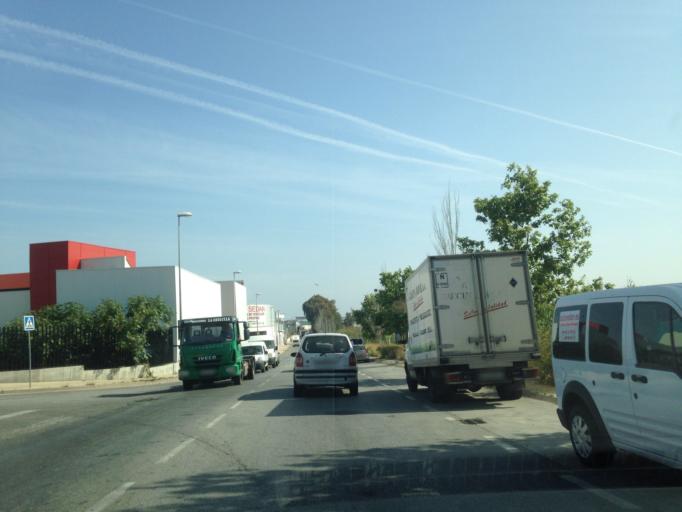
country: ES
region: Andalusia
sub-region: Provincia de Malaga
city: Malaga
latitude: 36.7126
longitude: -4.4728
